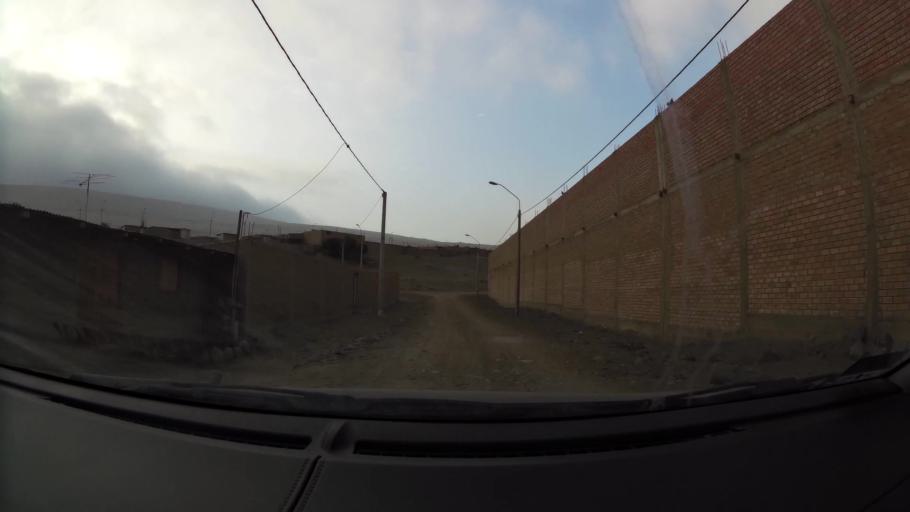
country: PE
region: Lima
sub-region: Lima
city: Santa Rosa
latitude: -11.7345
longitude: -77.1371
